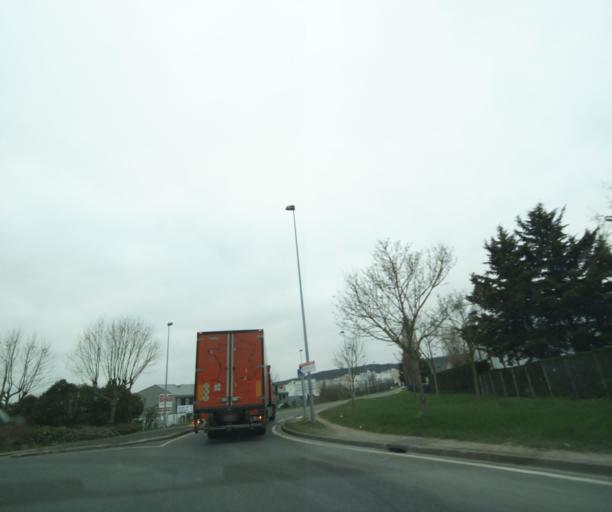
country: FR
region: Ile-de-France
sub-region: Departement des Yvelines
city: Chanteloup-les-Vignes
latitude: 48.9674
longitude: 2.0330
